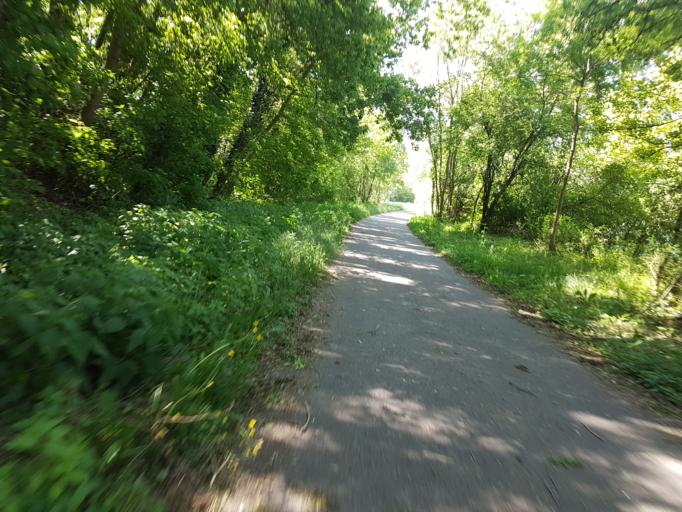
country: FR
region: Rhone-Alpes
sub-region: Departement de la Drome
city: Andancette
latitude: 45.2593
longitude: 4.8107
